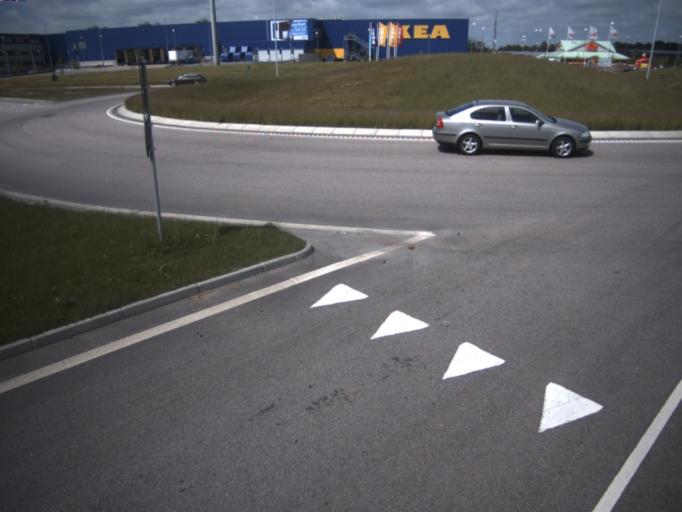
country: SE
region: Skane
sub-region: Helsingborg
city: Odakra
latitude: 56.0904
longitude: 12.7648
